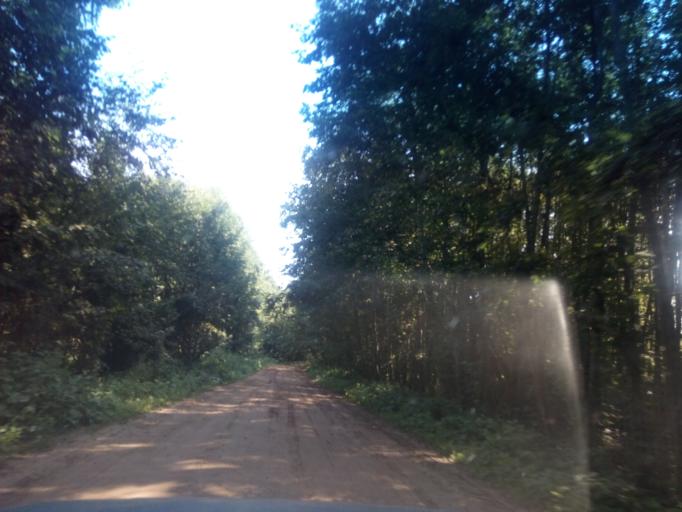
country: BY
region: Vitebsk
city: Dzisna
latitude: 55.6447
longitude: 28.3012
